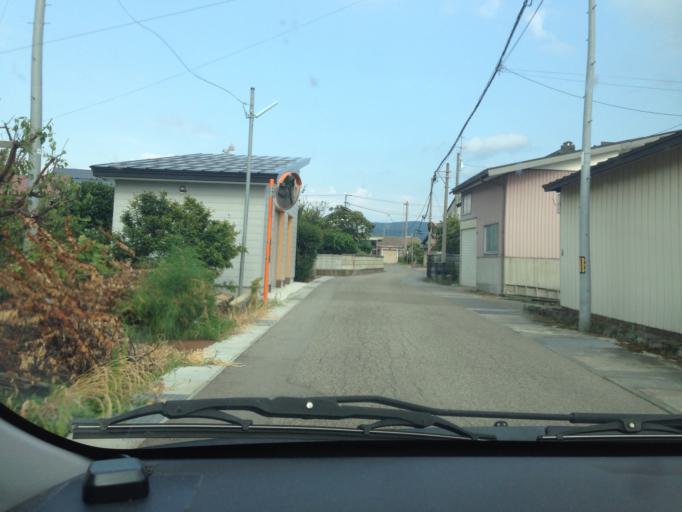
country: JP
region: Fukushima
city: Kitakata
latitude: 37.5171
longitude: 139.9161
